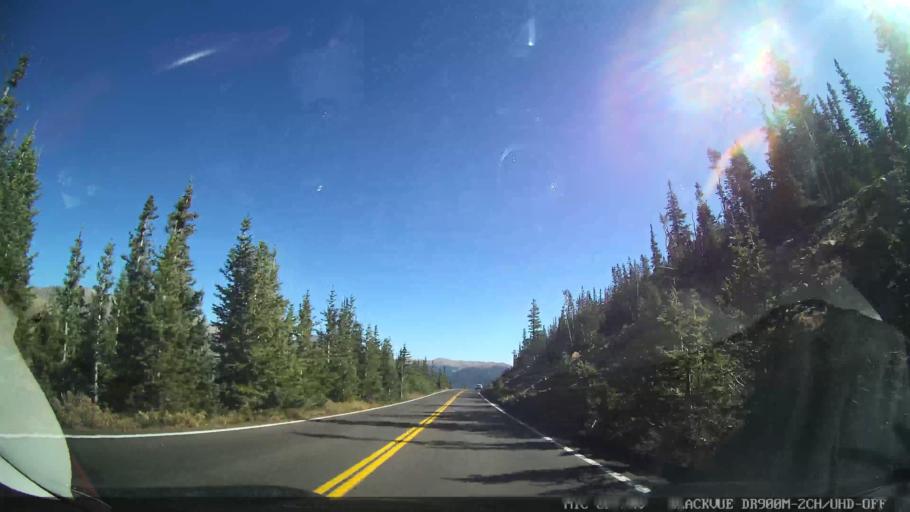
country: US
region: Colorado
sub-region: Larimer County
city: Estes Park
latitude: 40.3929
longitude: -105.6857
